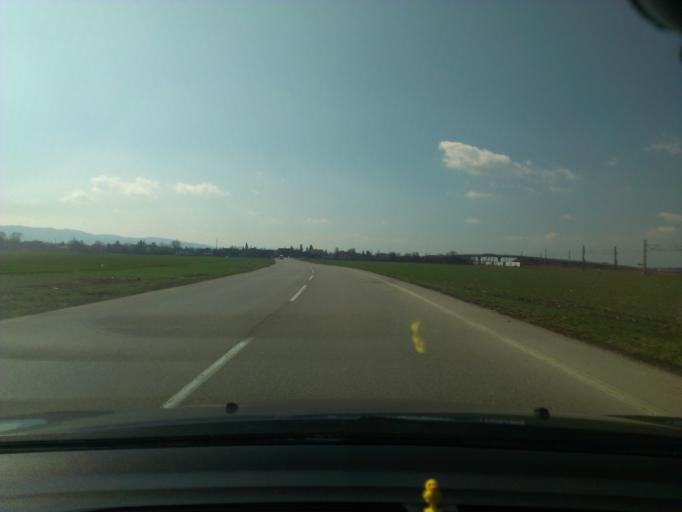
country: SK
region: Trnavsky
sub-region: Okres Trnava
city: Piestany
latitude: 48.6650
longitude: 17.8421
